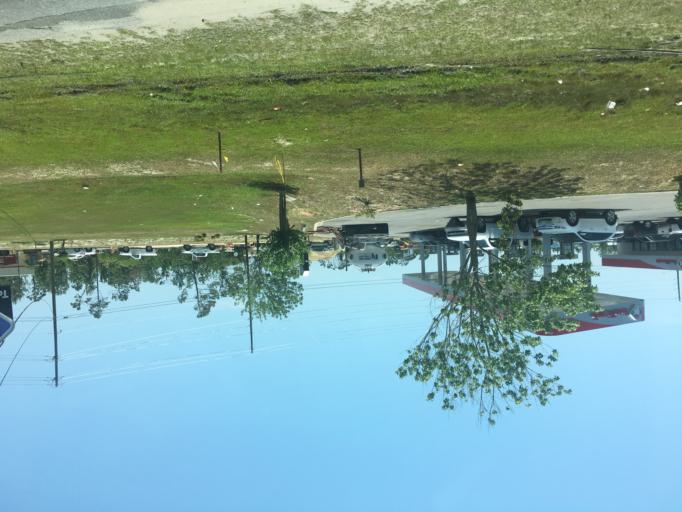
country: US
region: Florida
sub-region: Bay County
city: Lynn Haven
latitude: 30.2224
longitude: -85.6621
